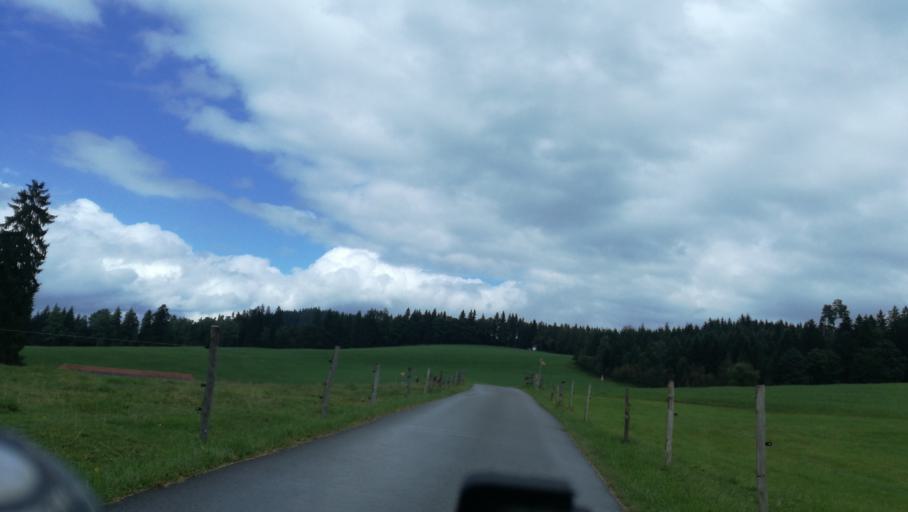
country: CH
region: Zug
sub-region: Zug
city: Walchwil
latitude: 47.1288
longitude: 8.5368
